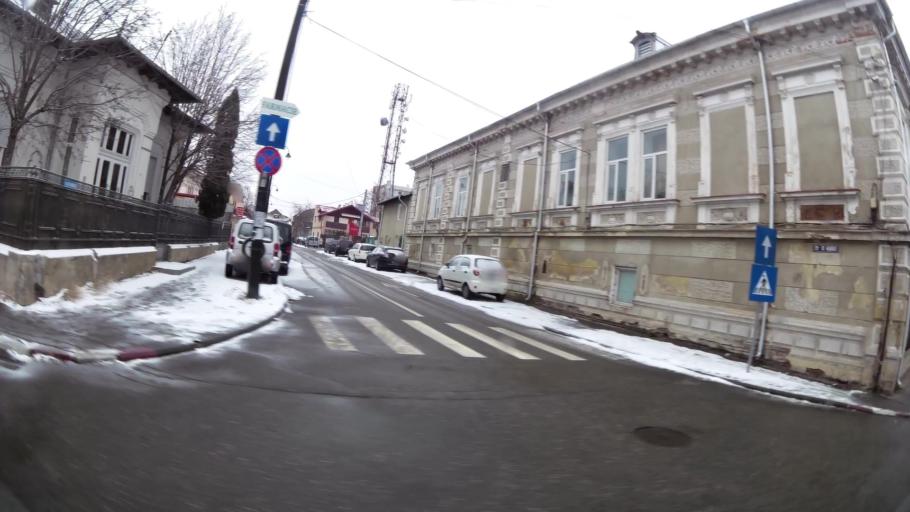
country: RO
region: Dambovita
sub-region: Municipiul Targoviste
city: Targoviste
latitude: 44.9281
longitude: 25.4563
